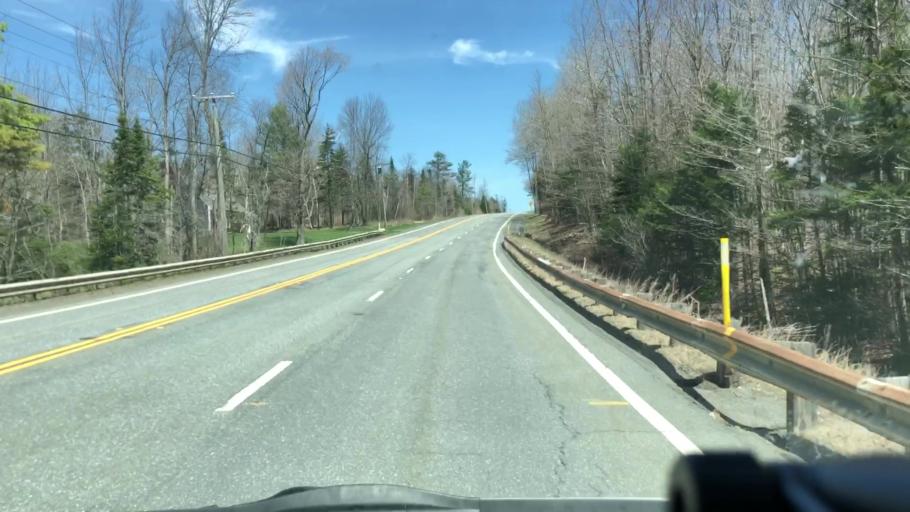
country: US
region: Massachusetts
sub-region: Berkshire County
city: Hinsdale
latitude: 42.5042
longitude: -73.0968
